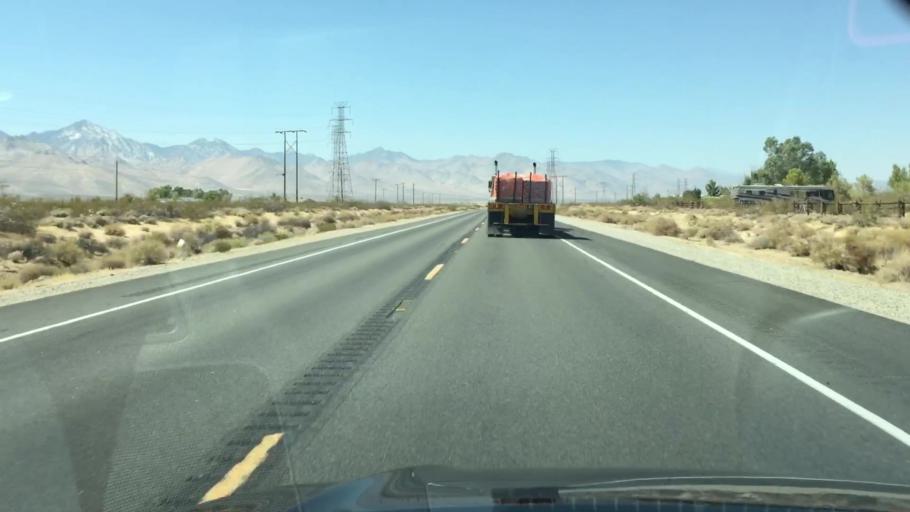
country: US
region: California
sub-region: Kern County
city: China Lake Acres
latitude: 35.6378
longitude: -117.7888
